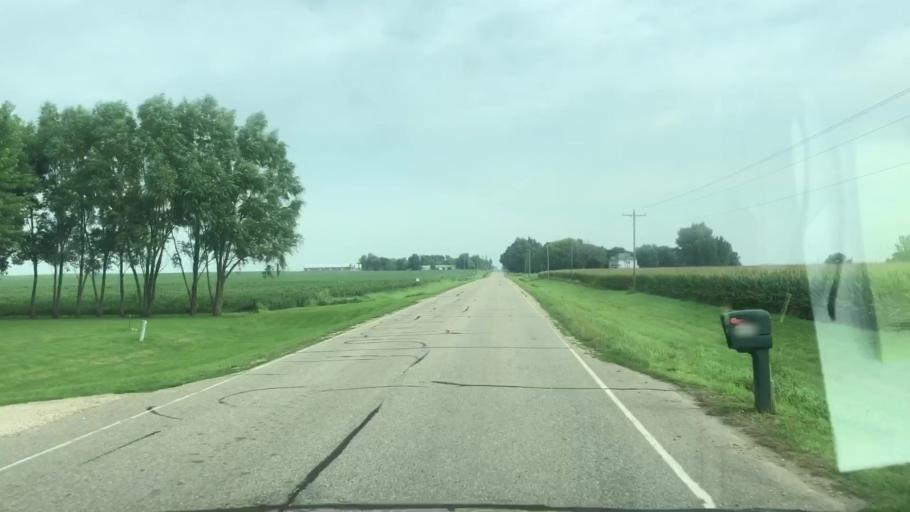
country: US
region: Iowa
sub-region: O'Brien County
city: Sheldon
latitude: 43.1973
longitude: -95.8622
